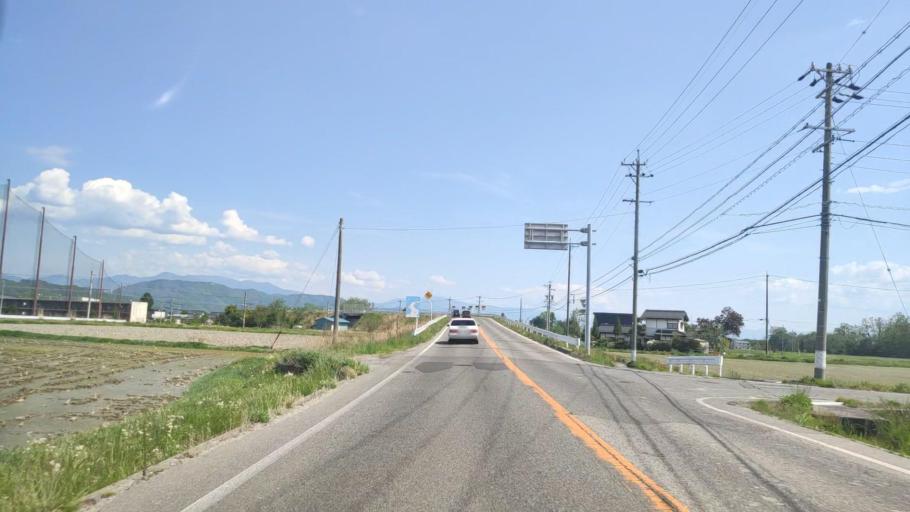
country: JP
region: Nagano
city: Hotaka
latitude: 36.3785
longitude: 137.8692
